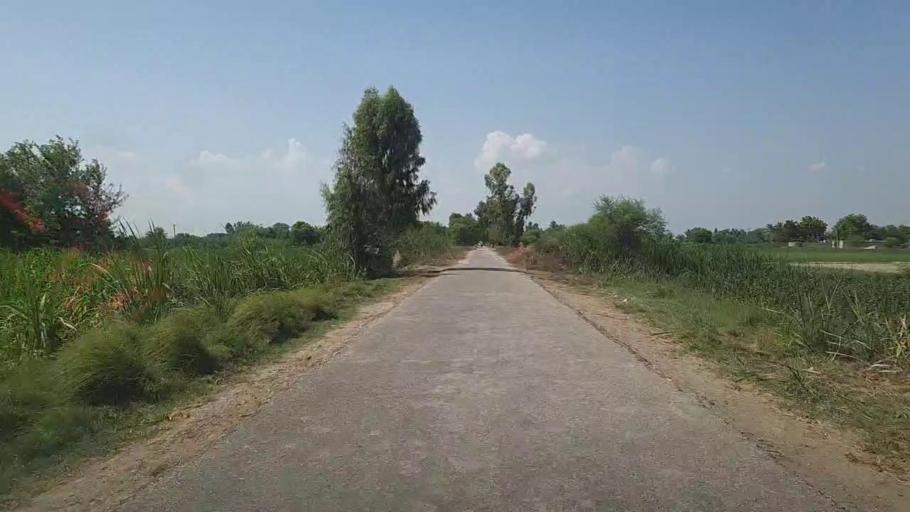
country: PK
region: Sindh
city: Khairpur
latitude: 28.0839
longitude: 69.6346
